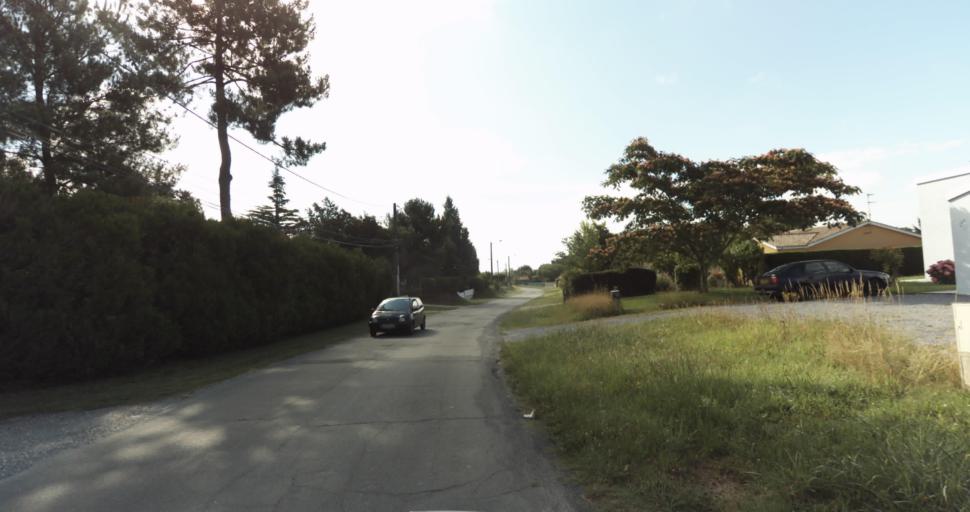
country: FR
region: Aquitaine
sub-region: Departement de la Gironde
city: Bazas
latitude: 44.4374
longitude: -0.2433
